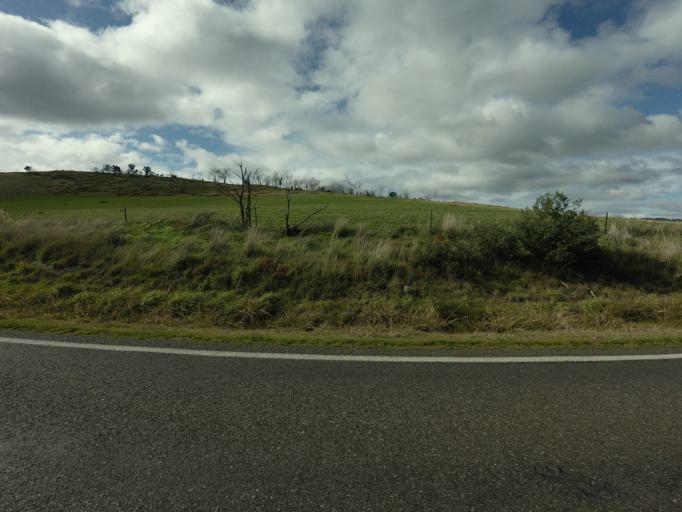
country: AU
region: Tasmania
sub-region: Derwent Valley
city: New Norfolk
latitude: -42.6554
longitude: 146.9350
